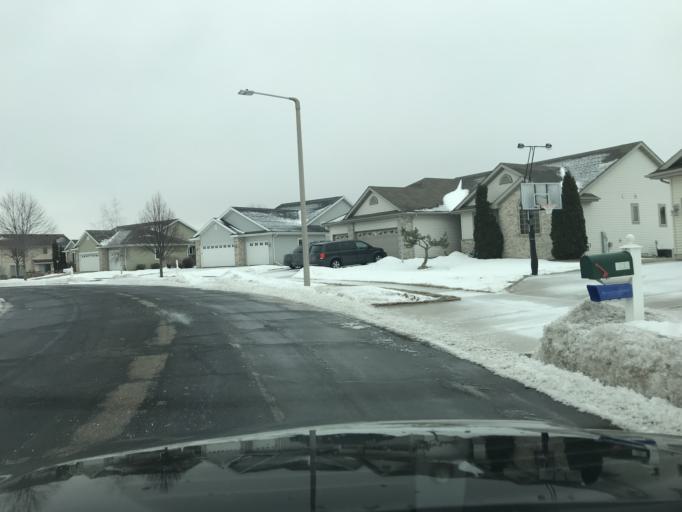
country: US
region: Wisconsin
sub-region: Dane County
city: Cottage Grove
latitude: 43.0922
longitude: -89.2127
